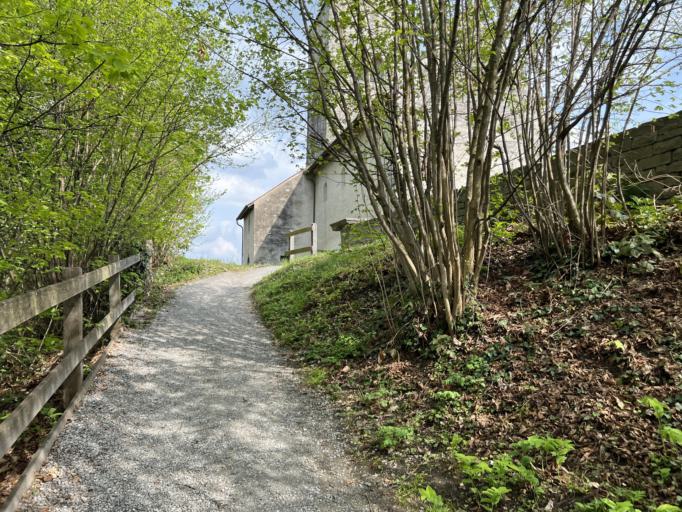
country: CH
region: Schwyz
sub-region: Bezirk Hoefe
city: Freienbach
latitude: 47.2181
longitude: 8.7784
